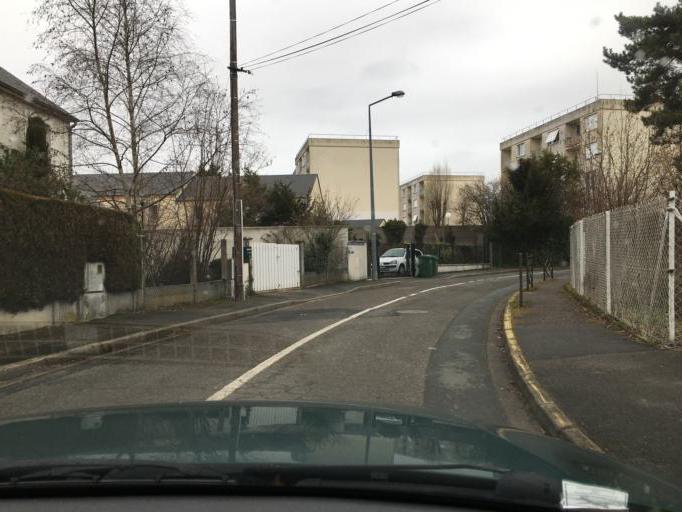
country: FR
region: Centre
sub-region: Departement du Loiret
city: Orleans
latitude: 47.9083
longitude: 1.9158
